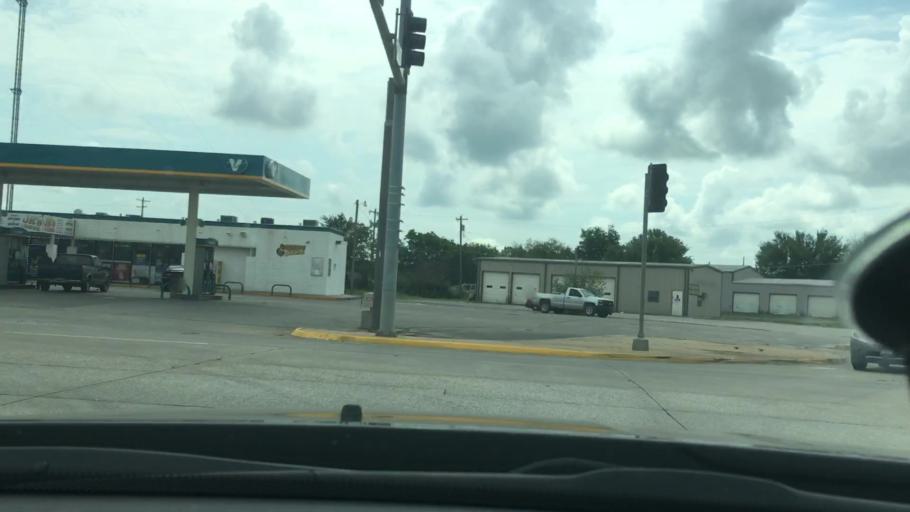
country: US
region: Oklahoma
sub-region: Carter County
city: Ardmore
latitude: 34.1855
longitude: -97.1082
